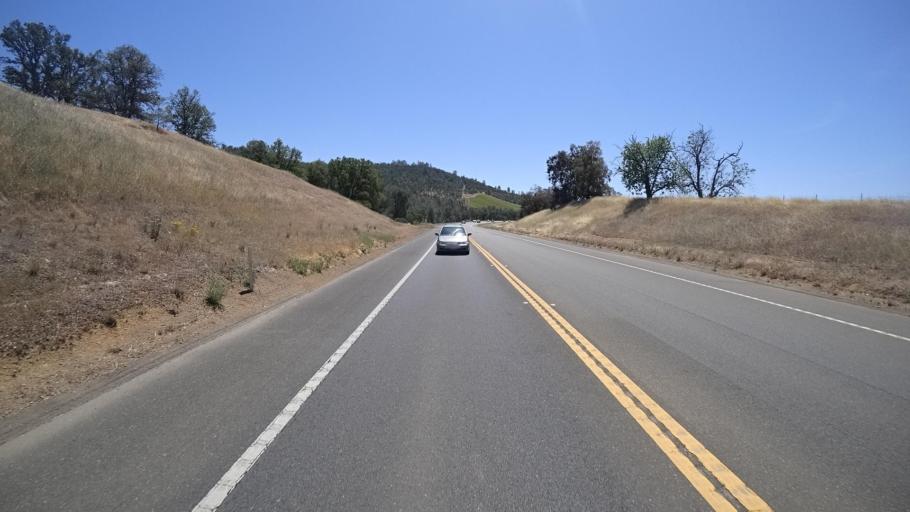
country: US
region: California
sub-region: Lake County
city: Clearlake
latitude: 38.9738
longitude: -122.6126
